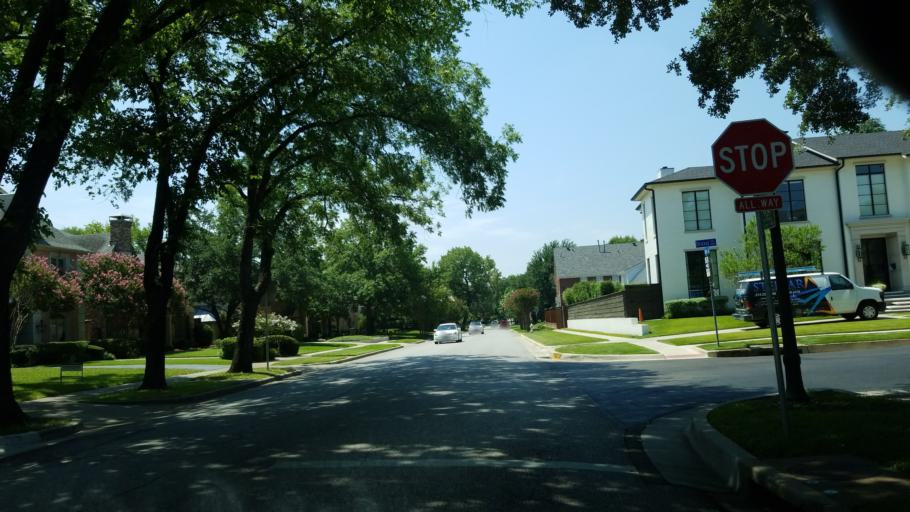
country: US
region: Texas
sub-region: Dallas County
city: Highland Park
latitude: 32.8357
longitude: -96.7817
